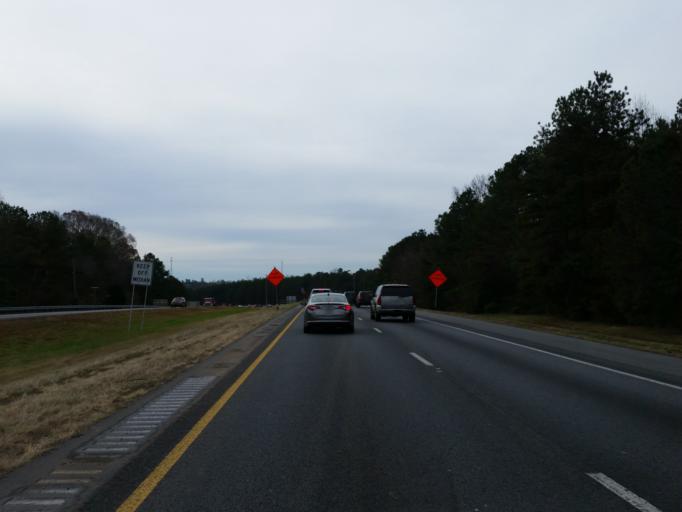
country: US
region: Georgia
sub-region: Cobb County
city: Marietta
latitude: 34.0038
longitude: -84.5612
